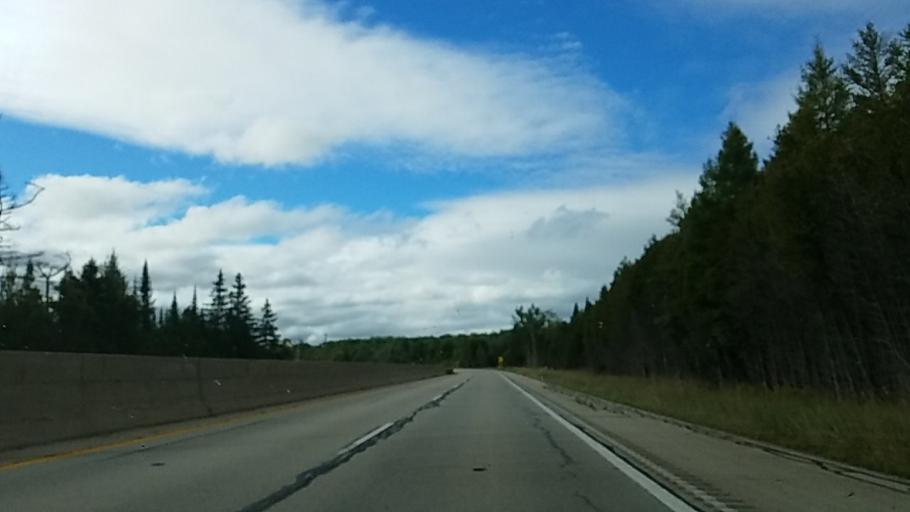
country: US
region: Michigan
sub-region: Mackinac County
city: Saint Ignace
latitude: 45.7692
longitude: -84.7351
